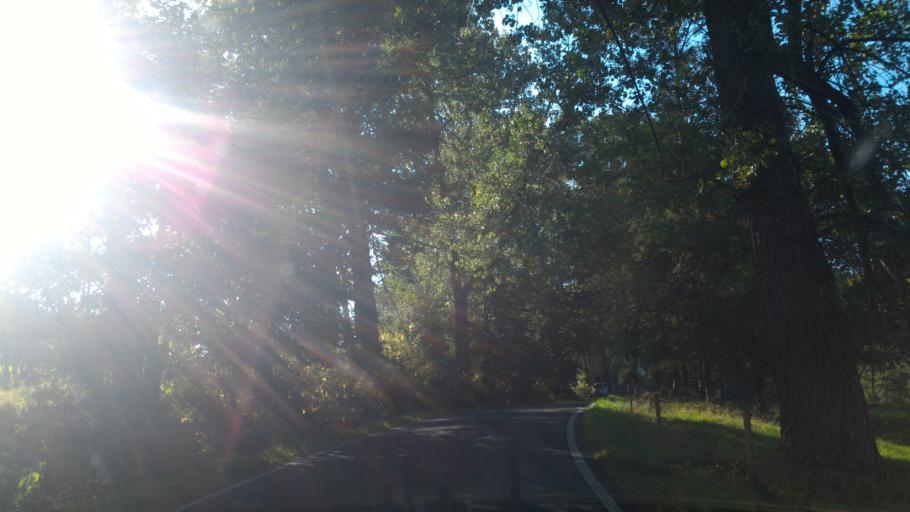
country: DE
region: Saxony
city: Kurort Jonsdorf
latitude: 50.8336
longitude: 14.6611
